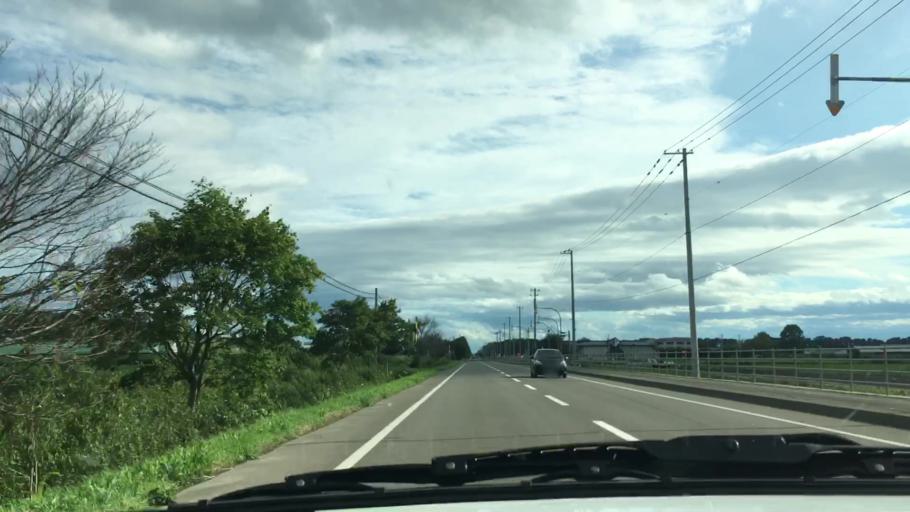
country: JP
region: Hokkaido
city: Otofuke
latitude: 43.2561
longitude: 143.3003
